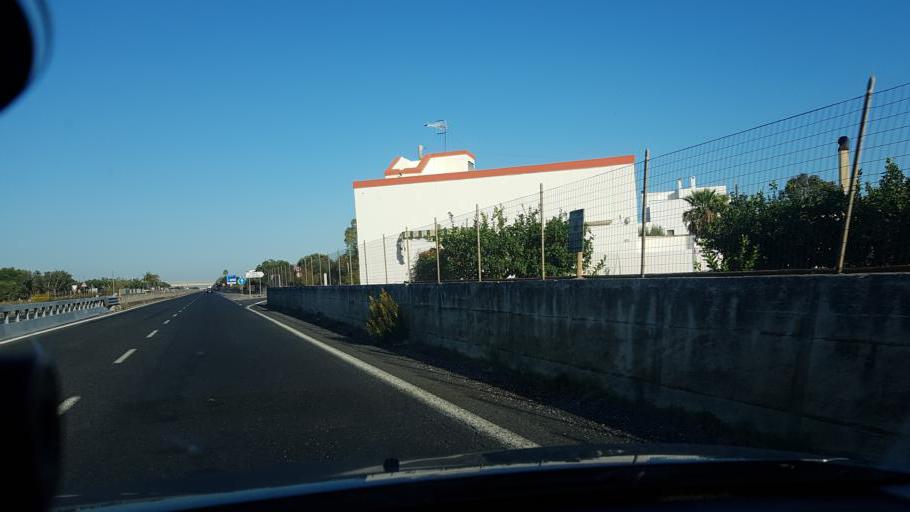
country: IT
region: Apulia
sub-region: Provincia di Bari
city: Monopoli
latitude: 40.9273
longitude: 17.3085
